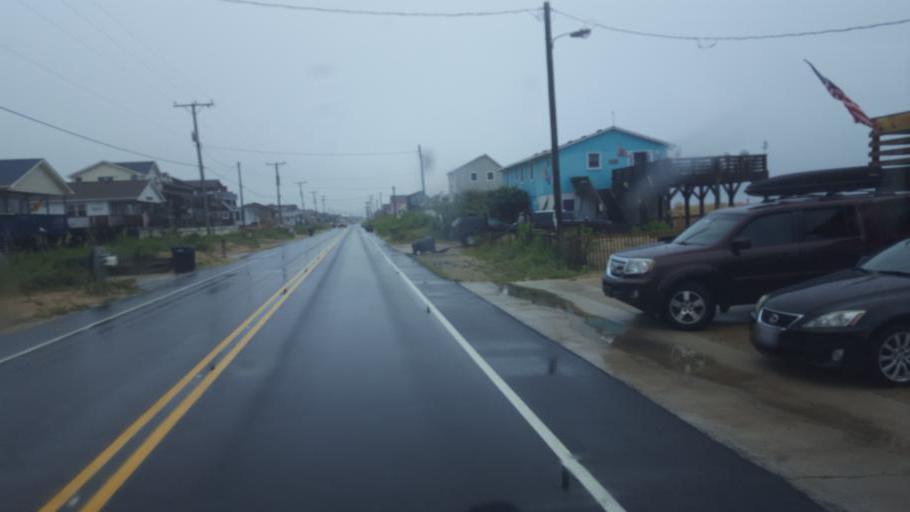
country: US
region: North Carolina
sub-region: Dare County
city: Kitty Hawk
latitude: 36.0742
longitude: -75.6953
